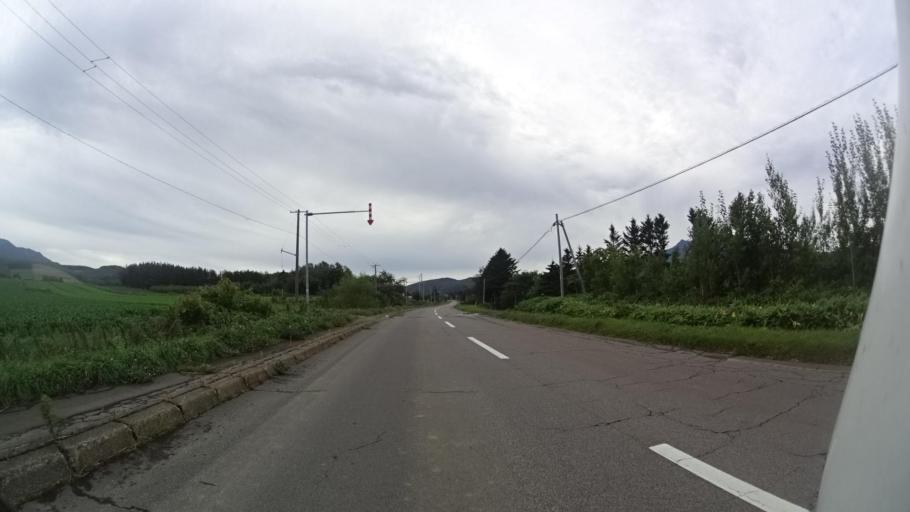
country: JP
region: Hokkaido
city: Shibetsu
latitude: 43.8728
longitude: 144.7484
